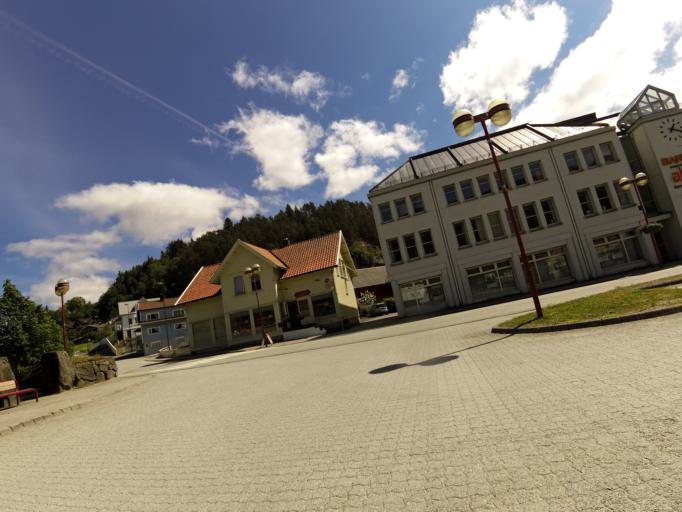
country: NO
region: Vest-Agder
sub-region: Kvinesdal
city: Liknes
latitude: 58.3166
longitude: 6.9626
